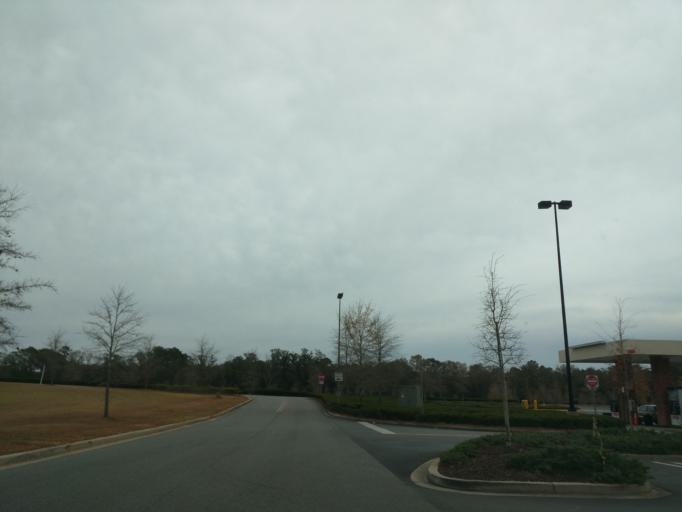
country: US
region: Florida
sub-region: Leon County
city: Tallahassee
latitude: 30.4619
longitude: -84.2126
